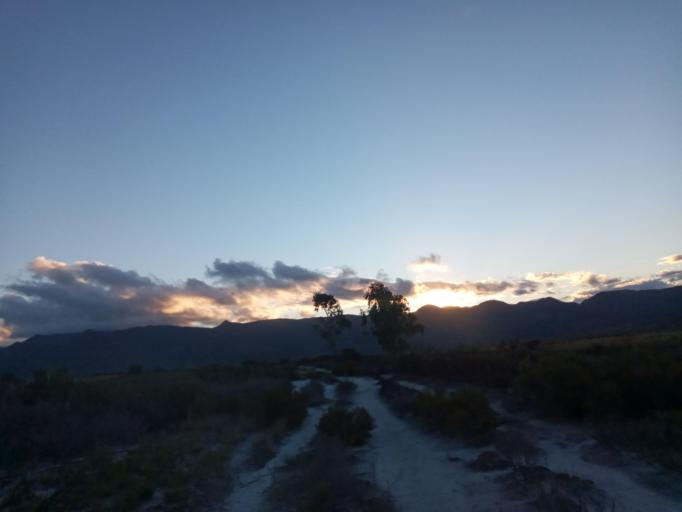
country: MG
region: Anosy
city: Fort Dauphin
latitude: -24.5138
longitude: 47.2332
